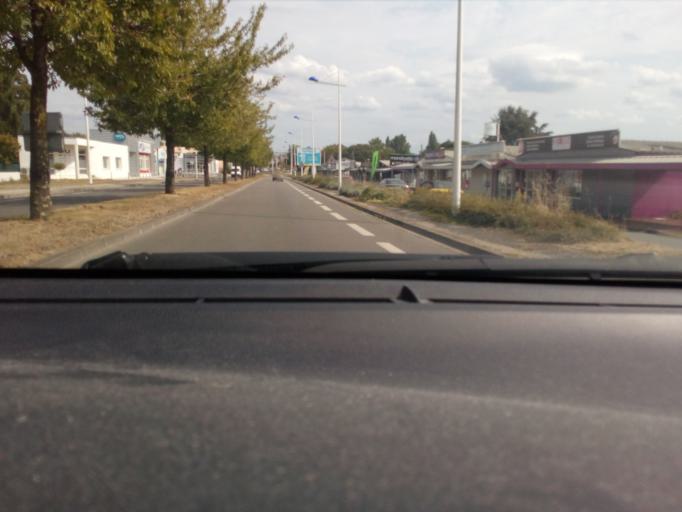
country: FR
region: Poitou-Charentes
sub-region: Departement de la Charente
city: Angouleme
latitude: 45.6634
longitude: 0.1538
